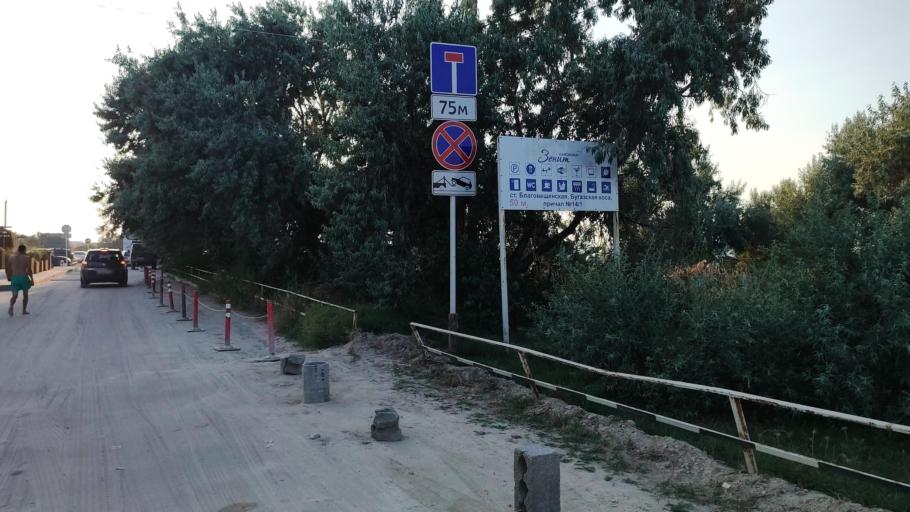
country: RU
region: Krasnodarskiy
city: Blagovetschenskaya
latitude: 45.0663
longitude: 37.0415
